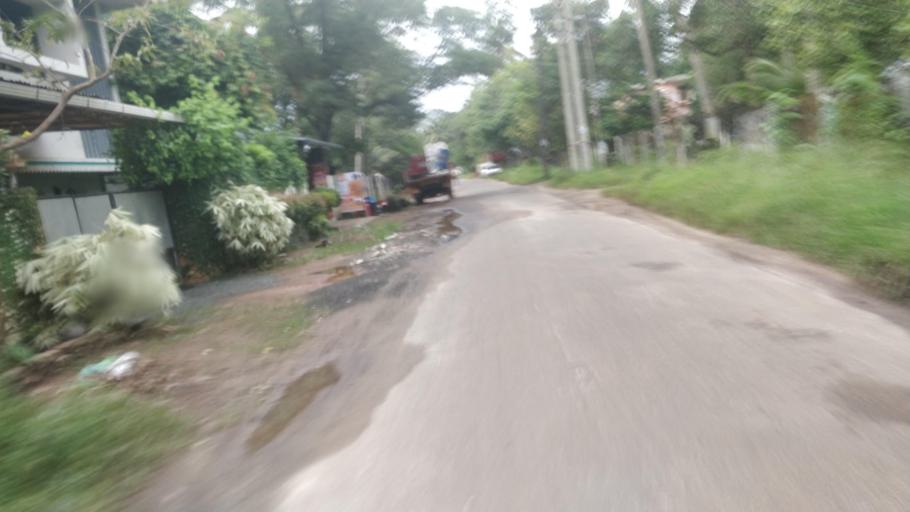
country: IN
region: Kerala
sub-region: Alappuzha
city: Vayalar
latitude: 9.6994
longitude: 76.3476
